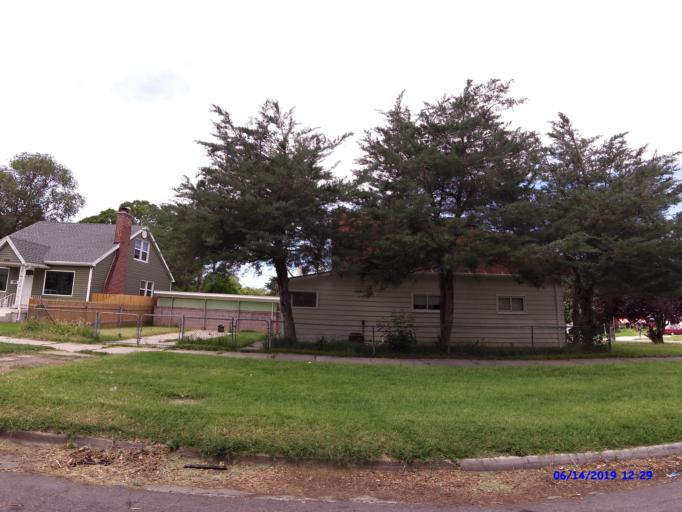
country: US
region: Utah
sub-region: Weber County
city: Ogden
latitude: 41.2264
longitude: -111.9509
